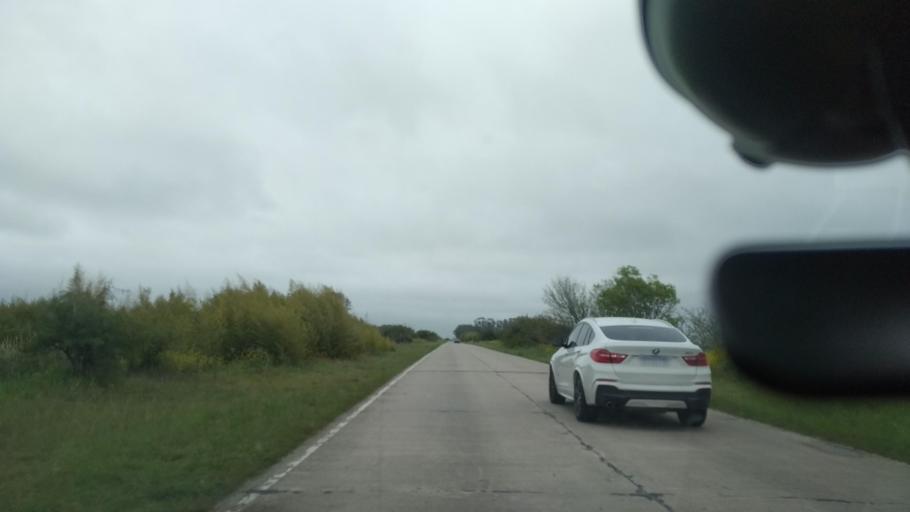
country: AR
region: Buenos Aires
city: Veronica
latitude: -35.5854
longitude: -57.2729
